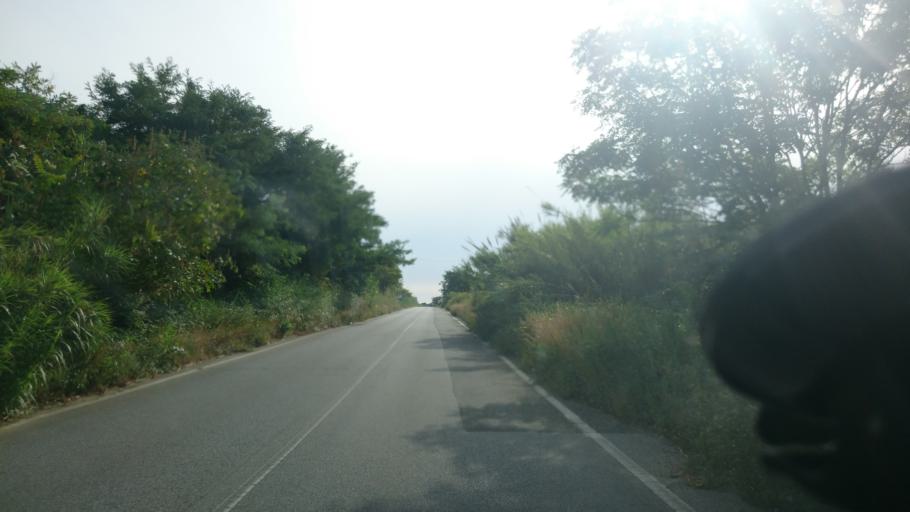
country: IT
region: Calabria
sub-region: Provincia di Vibo-Valentia
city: Parghelia
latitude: 38.6847
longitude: 15.9303
